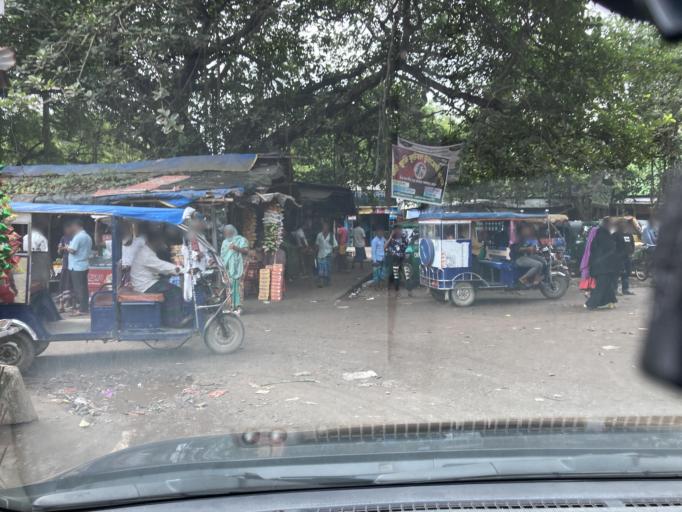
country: BD
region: Dhaka
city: Dohar
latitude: 23.7620
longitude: 90.1923
